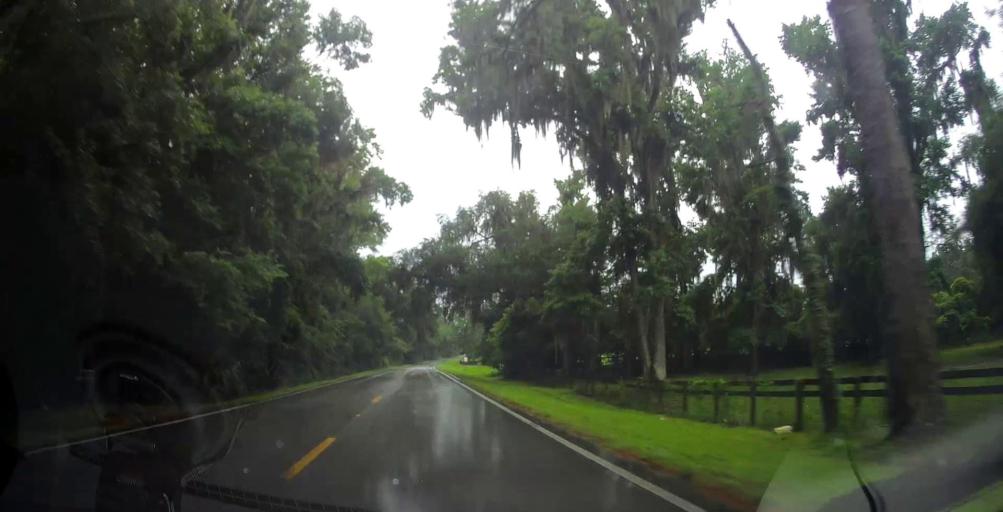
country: US
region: Florida
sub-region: Marion County
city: Citra
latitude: 29.3403
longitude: -82.2122
